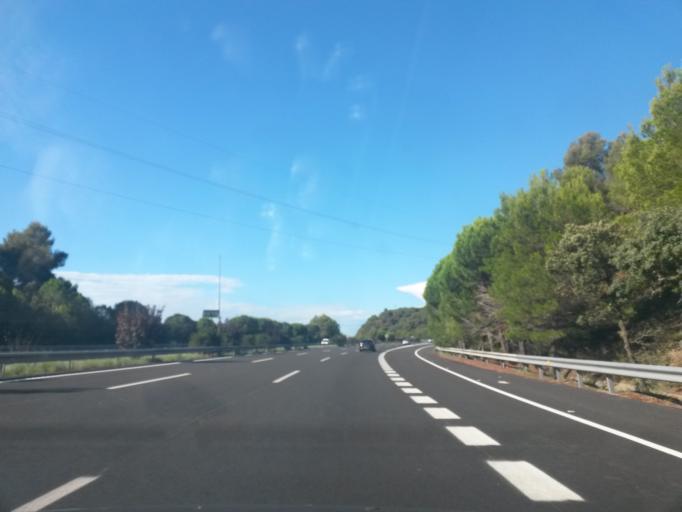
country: ES
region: Catalonia
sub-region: Provincia de Barcelona
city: Pineda de Mar
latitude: 41.6404
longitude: 2.6754
